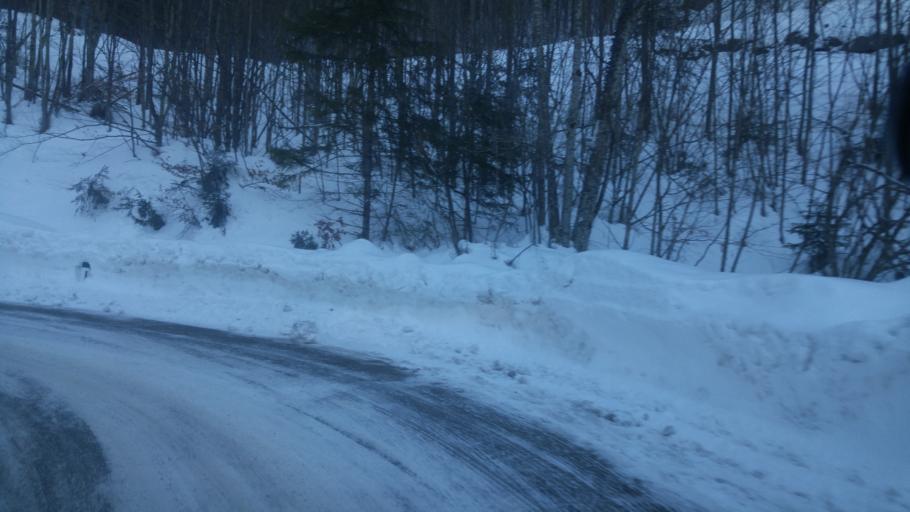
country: AT
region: Lower Austria
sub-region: Politischer Bezirk Lilienfeld
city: Hohenberg
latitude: 47.8789
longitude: 15.6209
